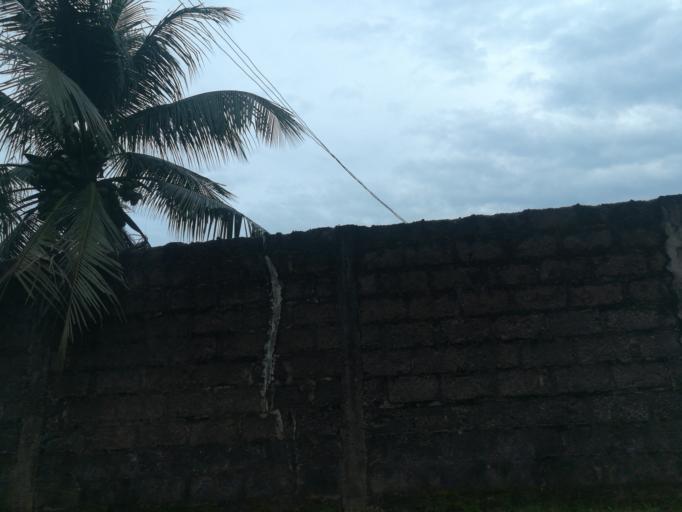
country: NG
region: Rivers
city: Port Harcourt
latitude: 4.7935
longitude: 6.9585
